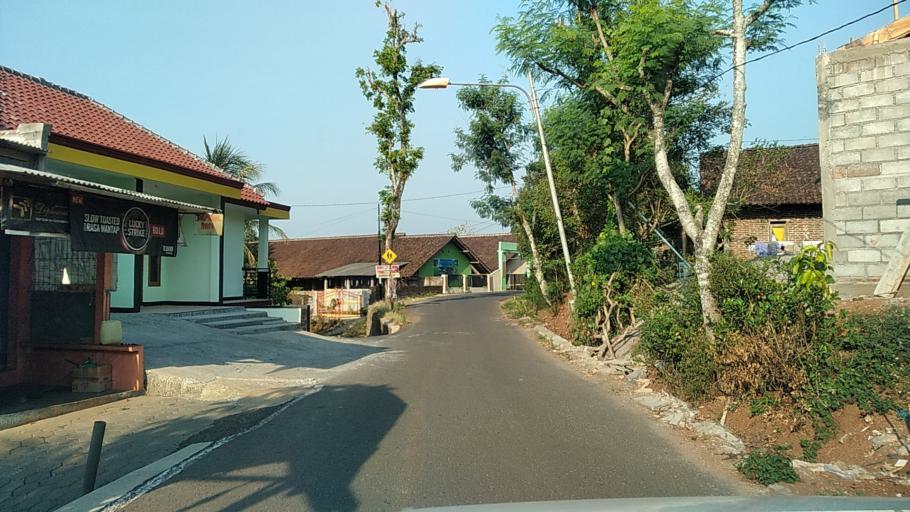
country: ID
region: Central Java
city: Ungaran
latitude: -7.0689
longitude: 110.3641
